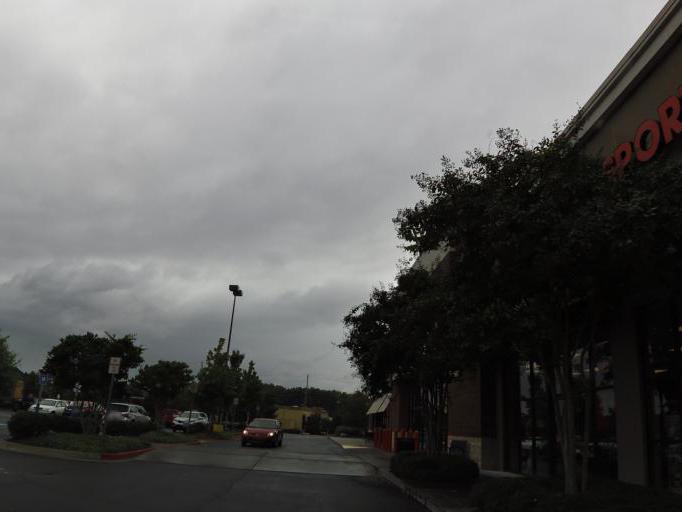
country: US
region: Georgia
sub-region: Cobb County
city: Acworth
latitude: 34.0381
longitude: -84.6853
